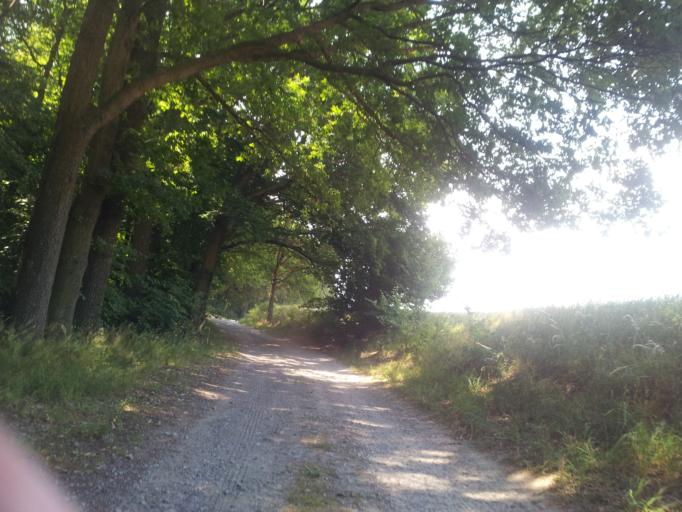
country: DE
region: Saxony
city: Panschwitz-Kuckau
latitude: 51.2104
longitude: 14.1999
